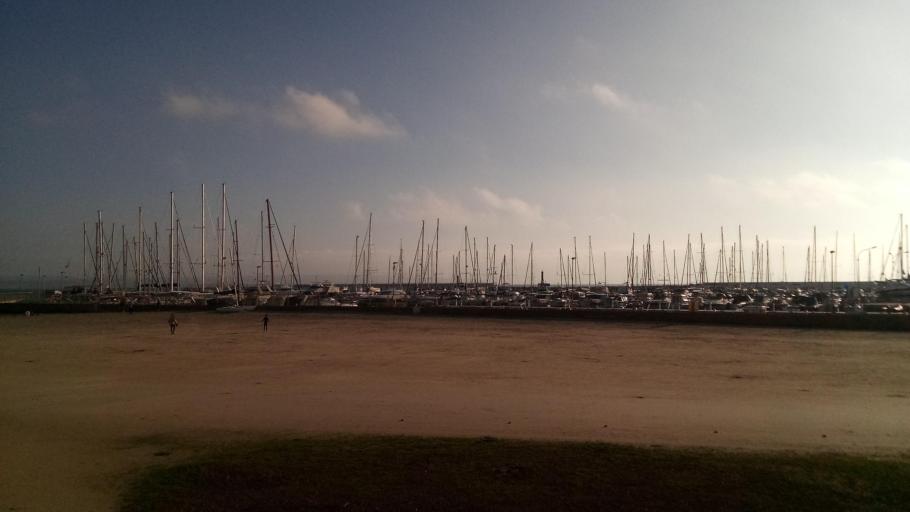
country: ES
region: Balearic Islands
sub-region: Illes Balears
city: s'Arenal
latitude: 39.5348
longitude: 2.7161
